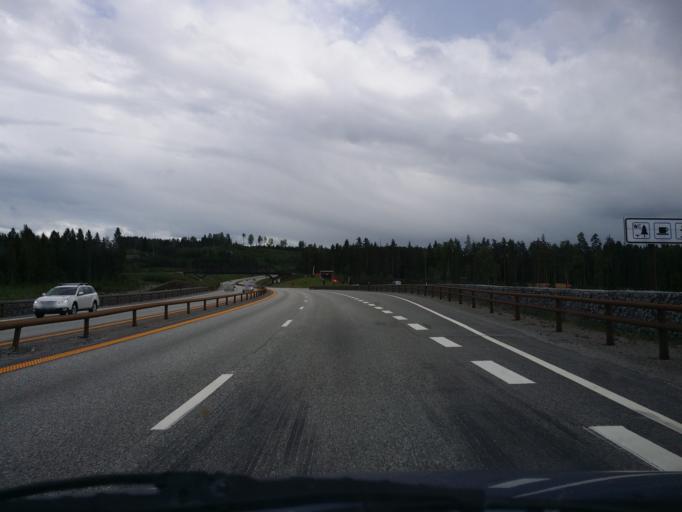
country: NO
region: Akershus
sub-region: Eidsvoll
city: Raholt
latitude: 60.2852
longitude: 11.1360
